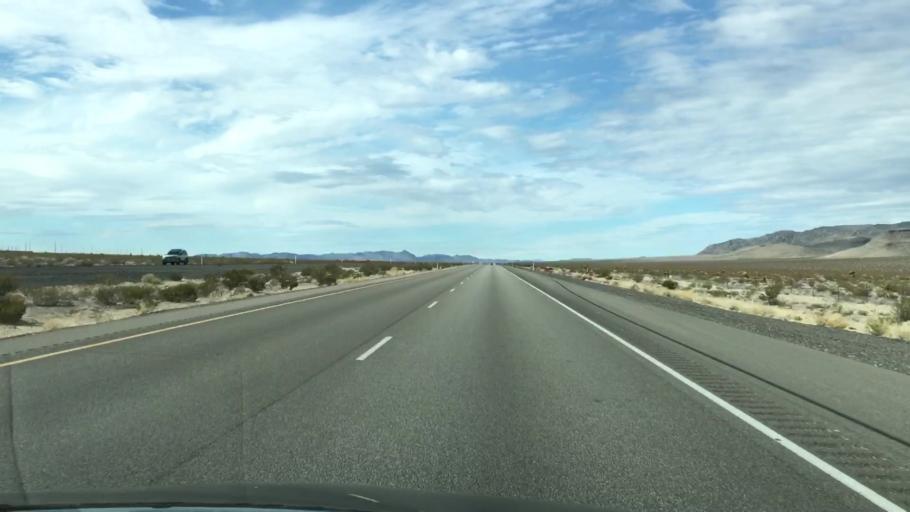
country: US
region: Nevada
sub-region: Nye County
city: Pahrump
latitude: 36.5861
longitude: -115.9151
